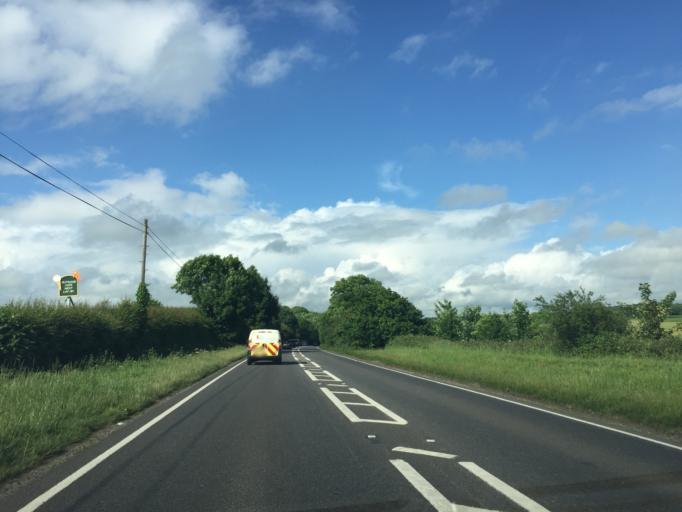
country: GB
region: England
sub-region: Dorset
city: Dorchester
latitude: 50.7287
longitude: -2.4059
